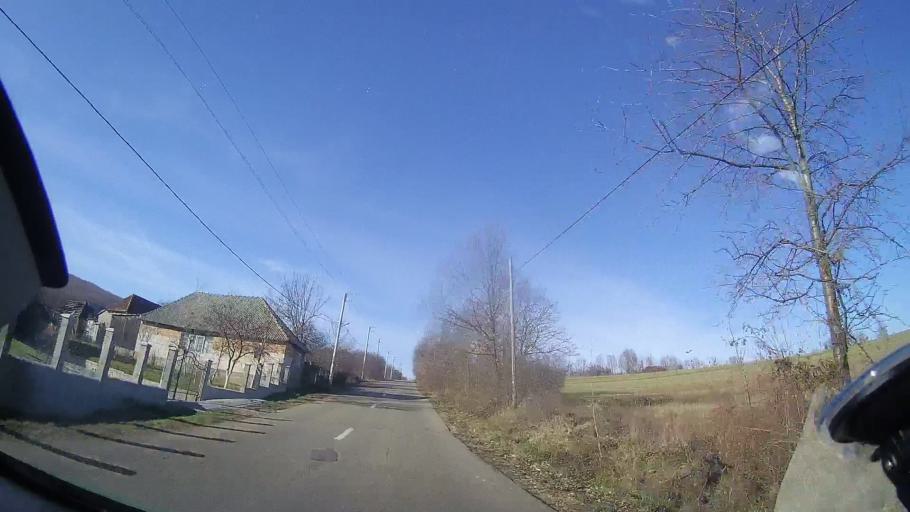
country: RO
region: Bihor
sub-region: Comuna Vadu Crisului
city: Vadu Crisului
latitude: 46.9728
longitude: 22.5429
